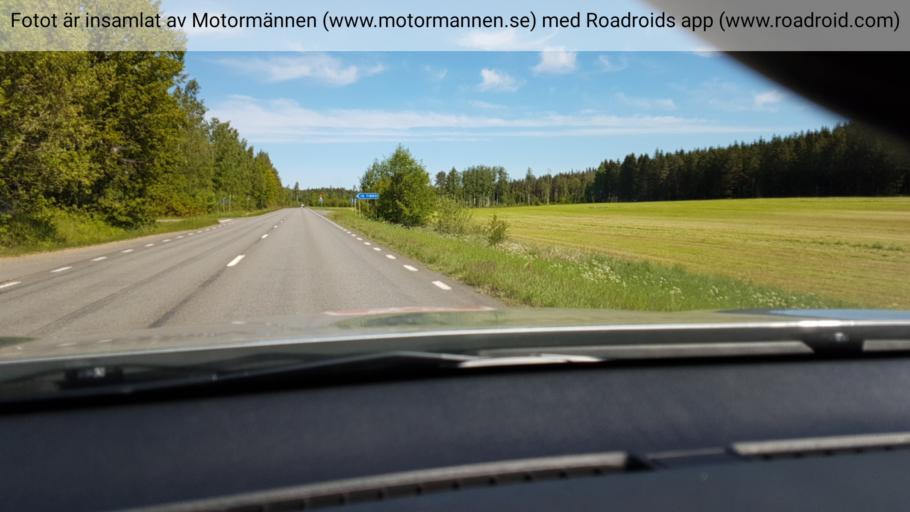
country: SE
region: Vaestra Goetaland
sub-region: Hjo Kommun
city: Hjo
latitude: 58.3819
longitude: 14.3520
